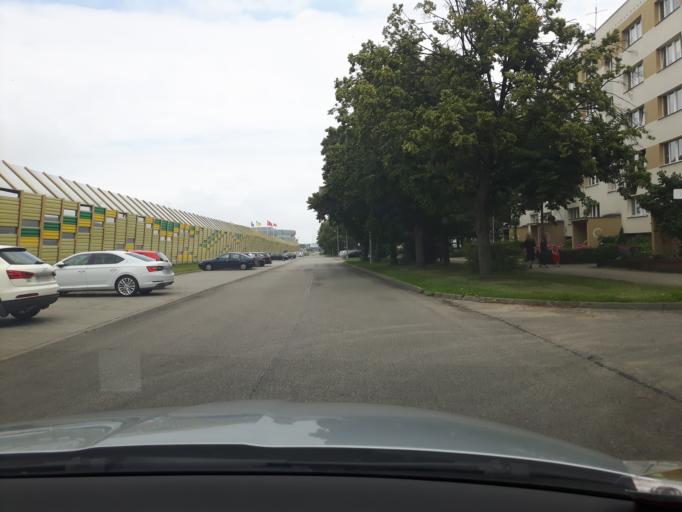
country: PL
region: Pomeranian Voivodeship
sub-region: Sopot
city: Sopot
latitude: 54.4233
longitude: 18.5728
